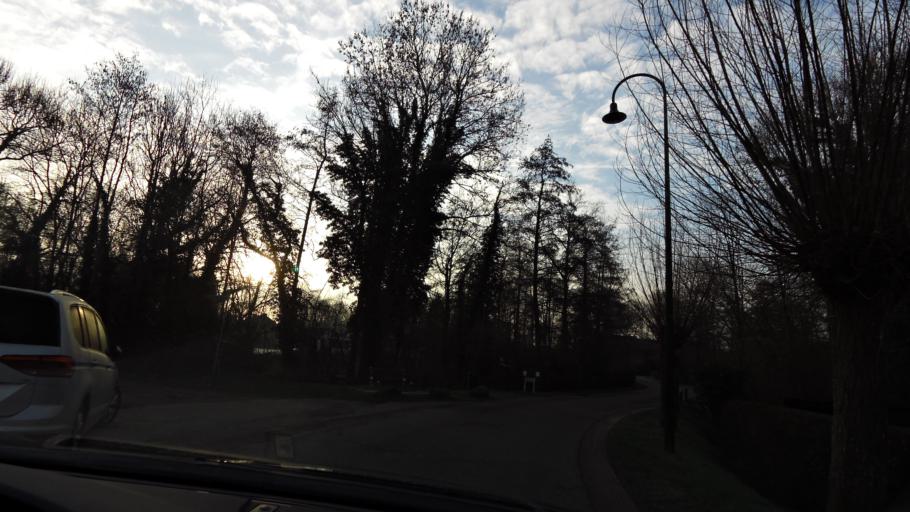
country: NL
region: Limburg
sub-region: Gemeente Nuth
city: Nuth
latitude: 50.9137
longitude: 5.8602
